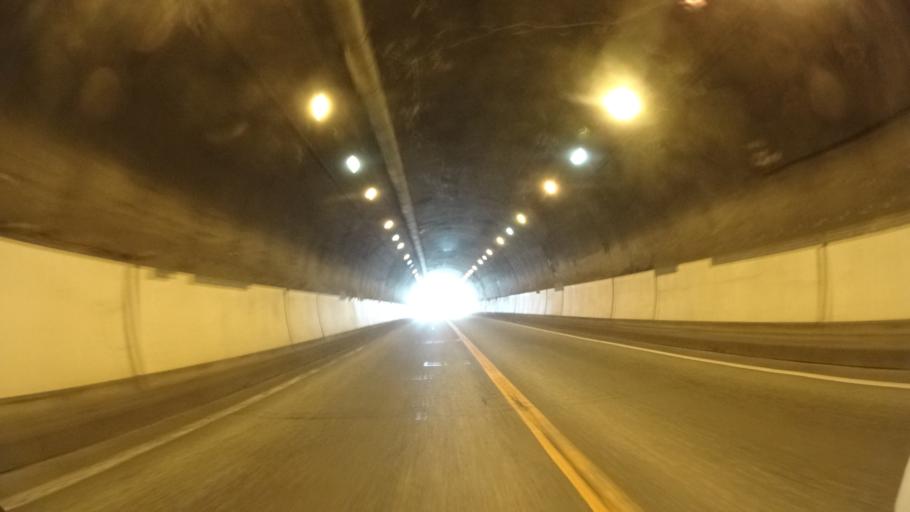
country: JP
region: Tottori
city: Tottori
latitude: 35.5209
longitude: 134.0857
